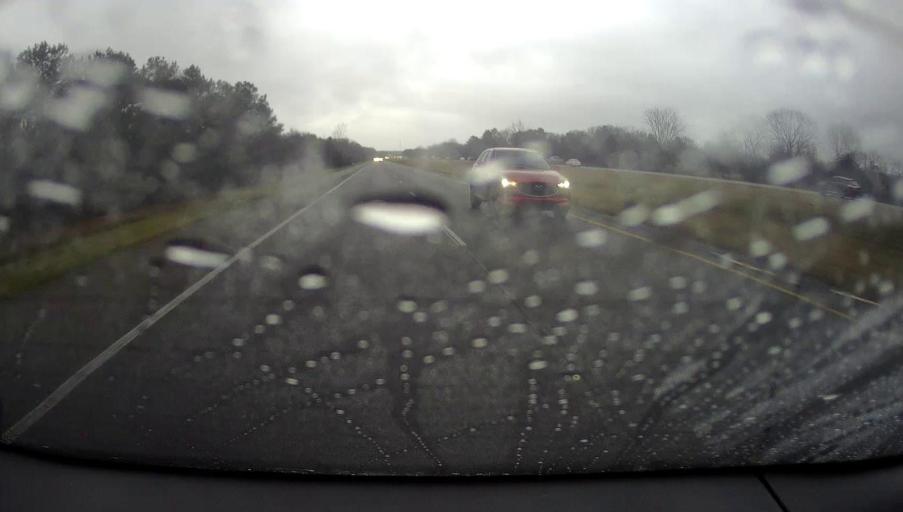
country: US
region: Alabama
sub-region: Morgan County
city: Falkville
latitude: 34.3915
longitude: -86.8957
